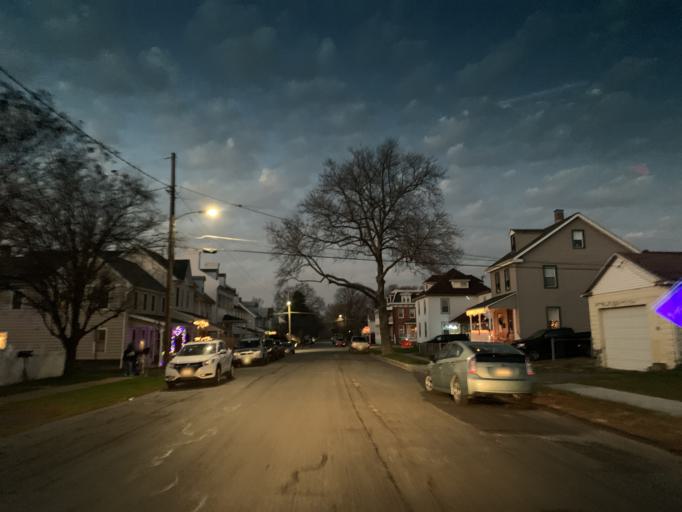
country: US
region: Maryland
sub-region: Harford County
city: Havre de Grace
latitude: 39.5520
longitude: -76.0953
